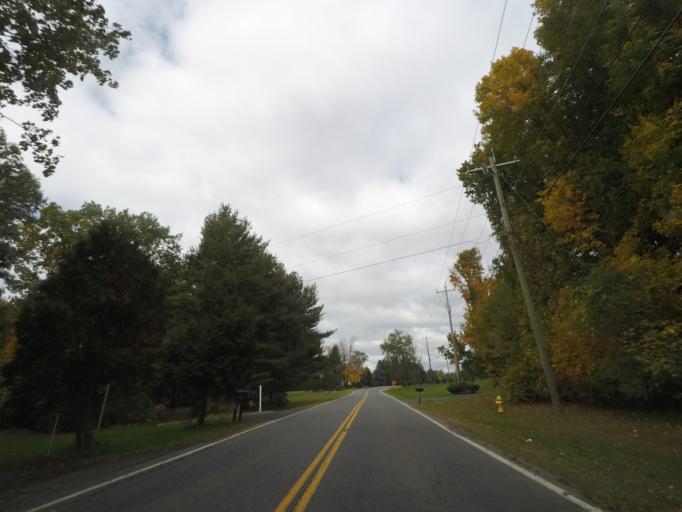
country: US
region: New York
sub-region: Saratoga County
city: Country Knolls
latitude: 42.8832
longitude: -73.7596
